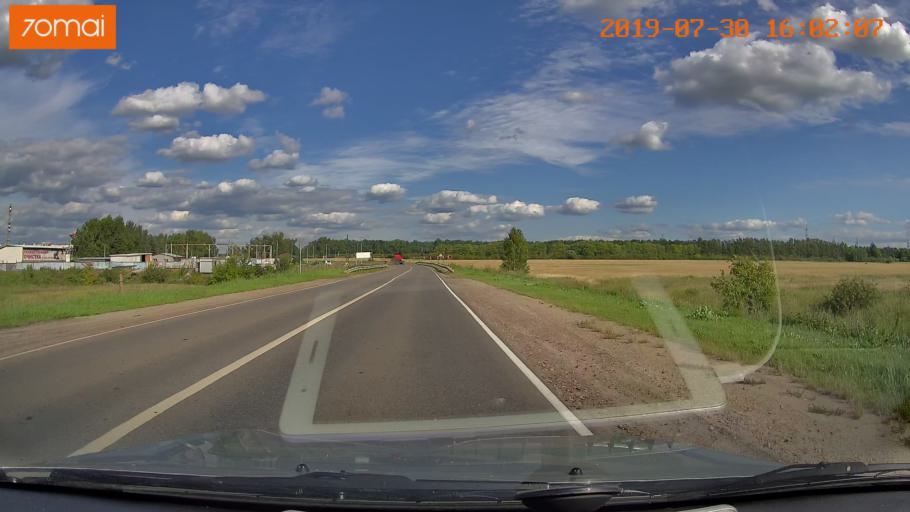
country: RU
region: Moskovskaya
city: Voskresensk
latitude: 55.2880
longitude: 38.6839
